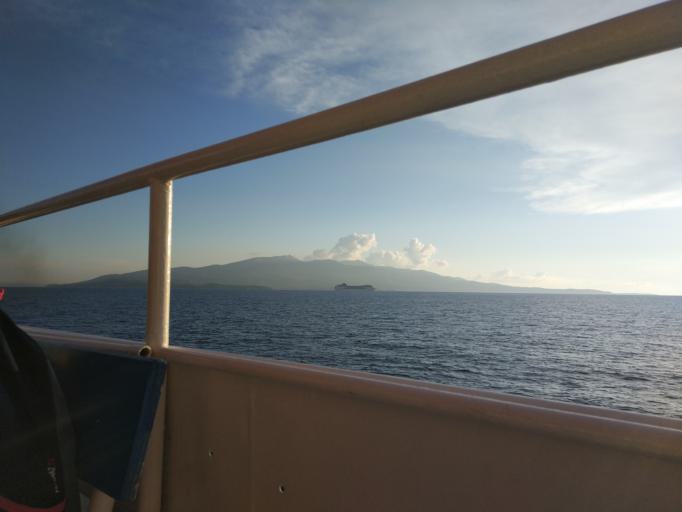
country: AL
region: Vlore
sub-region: Rrethi i Sarandes
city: Sarande
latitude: 39.8245
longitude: 19.9952
